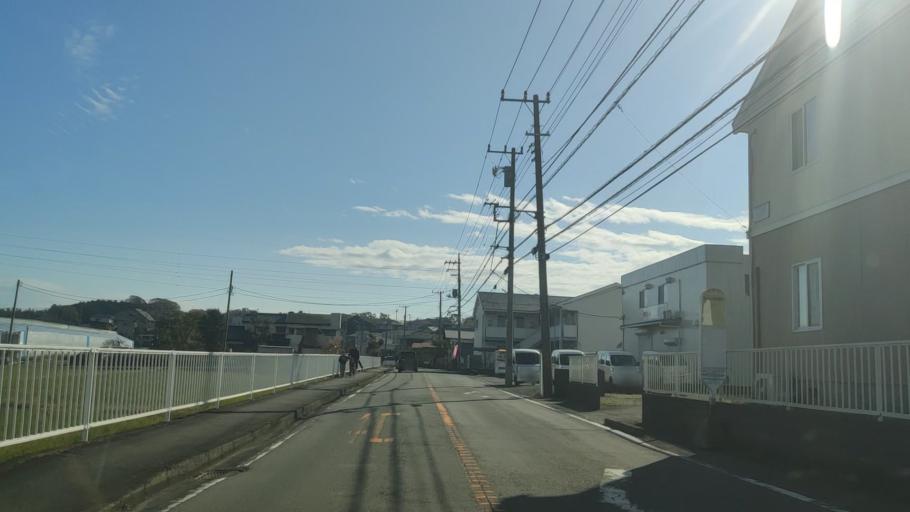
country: JP
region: Kanagawa
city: Atsugi
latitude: 35.4401
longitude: 139.3393
